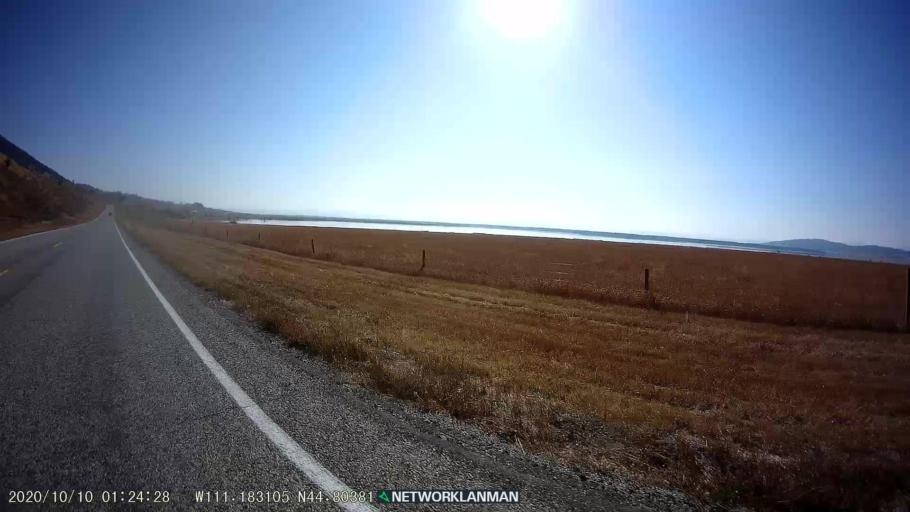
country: US
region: Montana
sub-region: Gallatin County
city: West Yellowstone
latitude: 44.8038
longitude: -111.1828
